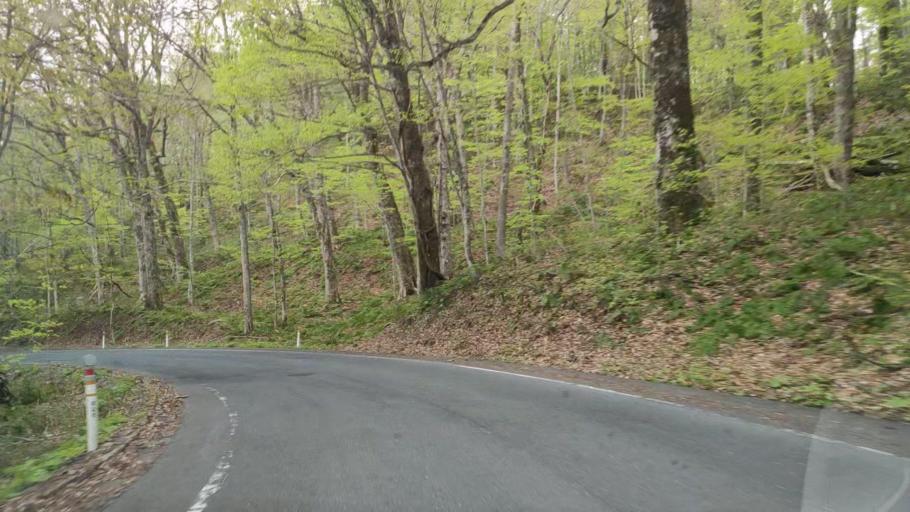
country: JP
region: Aomori
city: Aomori Shi
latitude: 40.5927
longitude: 140.9588
